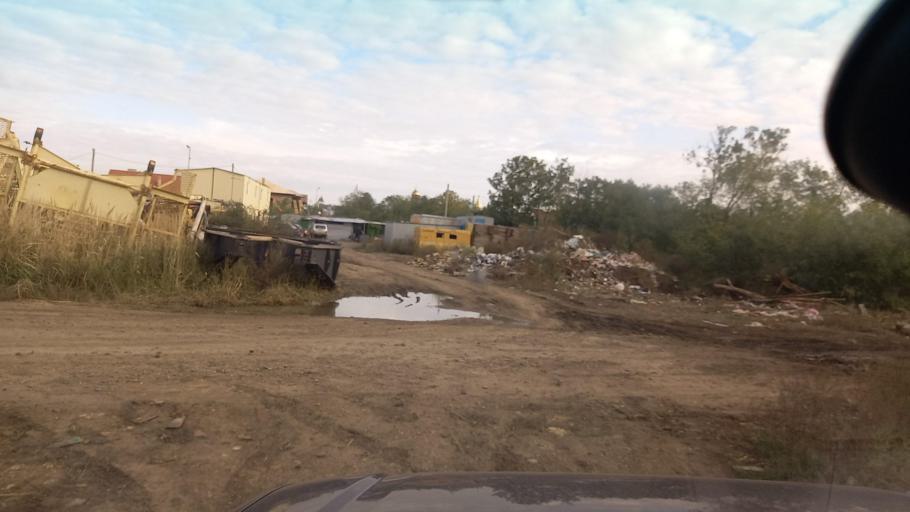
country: RU
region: Krasnodarskiy
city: Krasnodar
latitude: 45.1244
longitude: 38.9198
